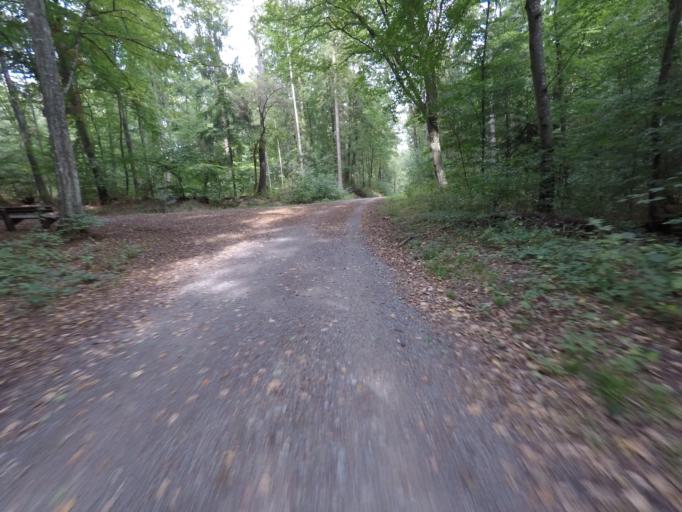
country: DE
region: Baden-Wuerttemberg
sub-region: Regierungsbezirk Stuttgart
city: Ehningen
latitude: 48.6710
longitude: 8.9762
